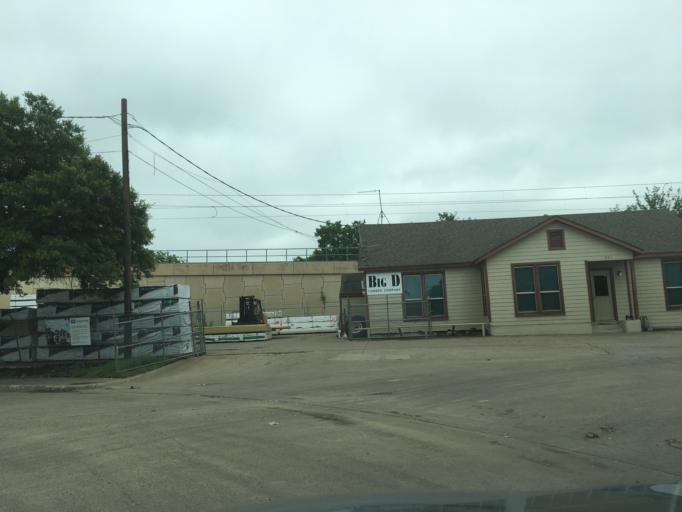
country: US
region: Texas
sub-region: Dallas County
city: Richardson
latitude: 32.9479
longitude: -96.7335
